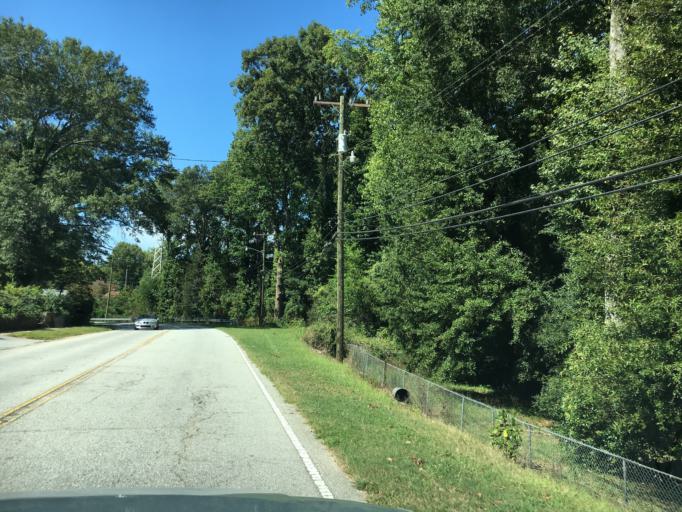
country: US
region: South Carolina
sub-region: Greenville County
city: Greer
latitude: 34.9322
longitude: -82.2341
